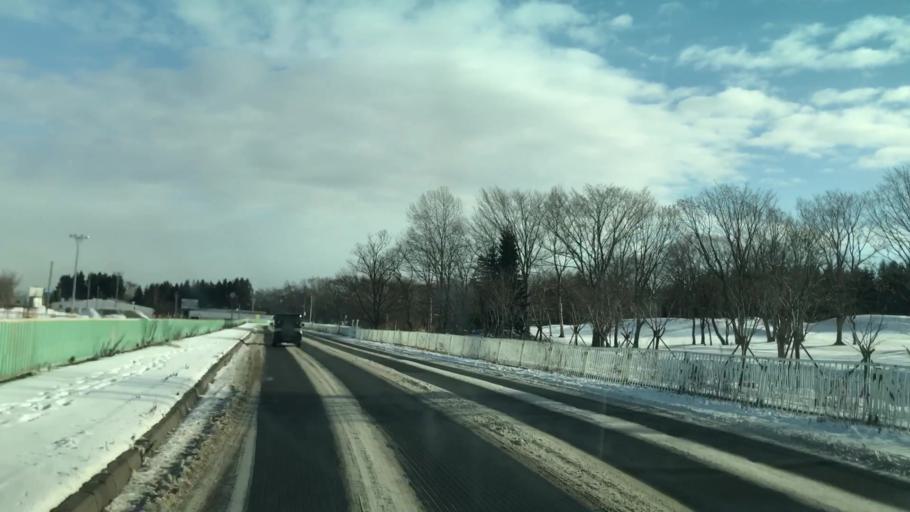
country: JP
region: Hokkaido
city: Chitose
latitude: 42.8120
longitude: 141.6437
